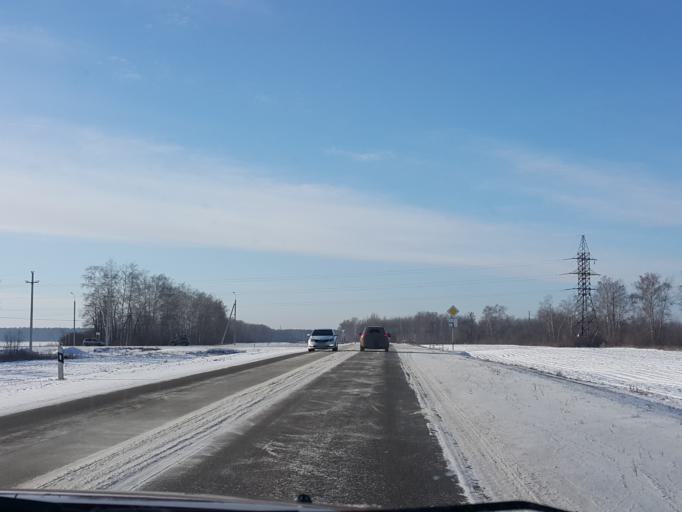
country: RU
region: Tambov
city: Znamenka
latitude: 52.4373
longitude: 41.4965
